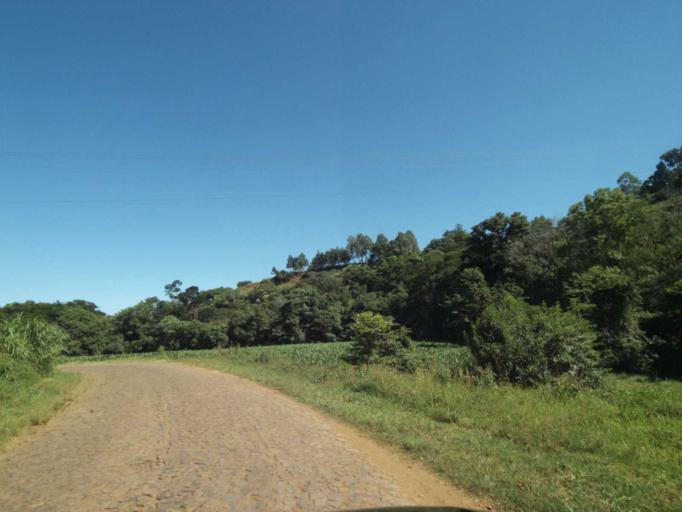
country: BR
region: Parana
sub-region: Francisco Beltrao
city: Francisco Beltrao
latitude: -26.1467
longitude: -53.3042
